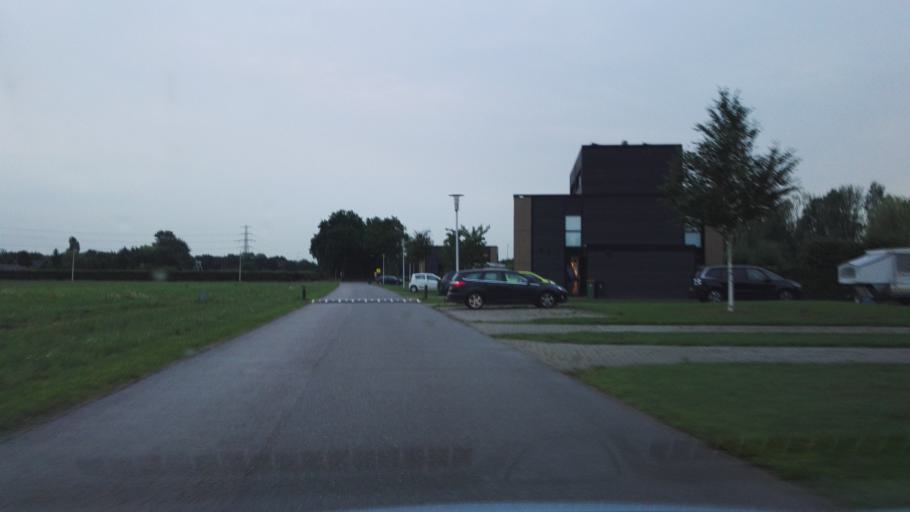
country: NL
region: Gelderland
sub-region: Gemeente Apeldoorn
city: Apeldoorn
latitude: 52.2022
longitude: 6.0112
